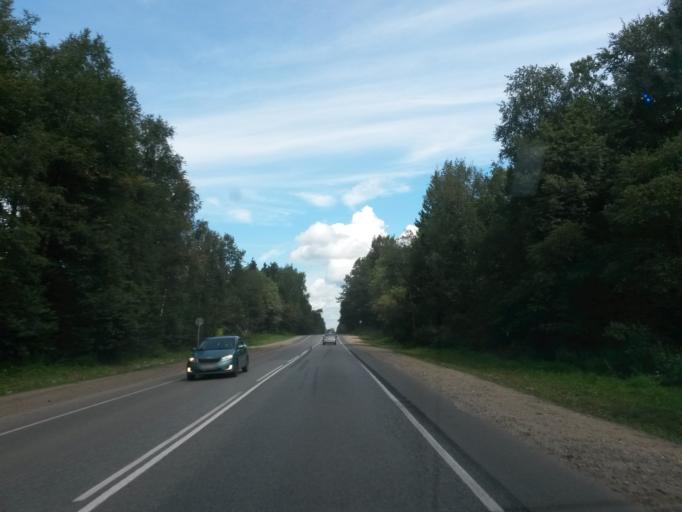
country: RU
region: Jaroslavl
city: Pereslavl'-Zalesskiy
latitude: 56.7995
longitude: 38.8928
